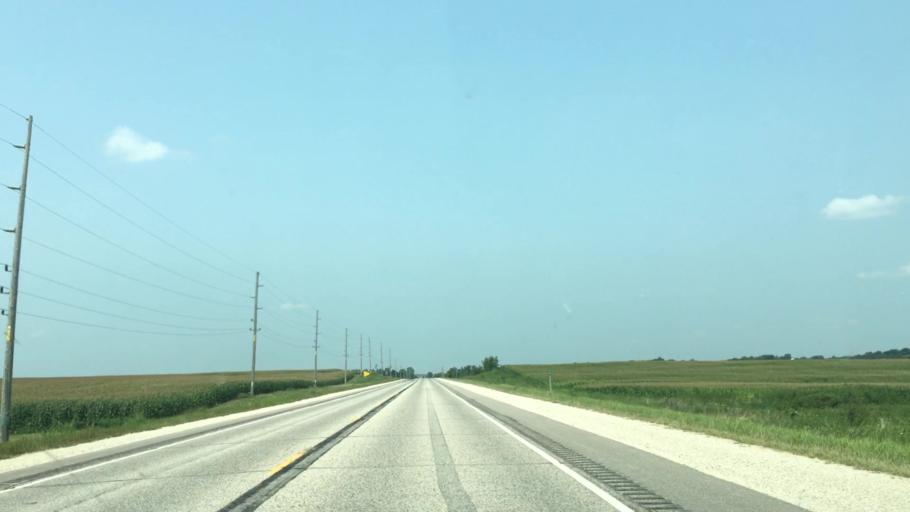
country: US
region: Iowa
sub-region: Fayette County
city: Fayette
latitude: 42.8860
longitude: -91.8104
